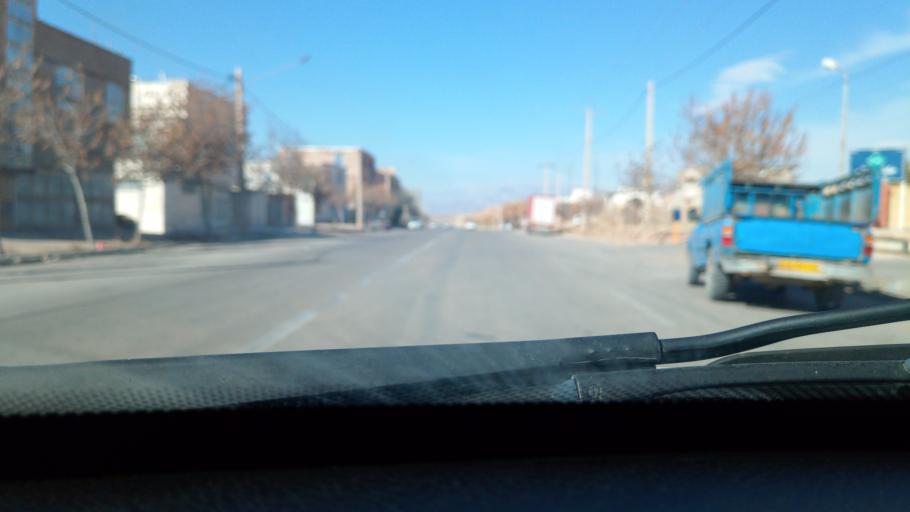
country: IR
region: Khorasan-e Shomali
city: Esfarayen
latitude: 37.0868
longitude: 57.4978
